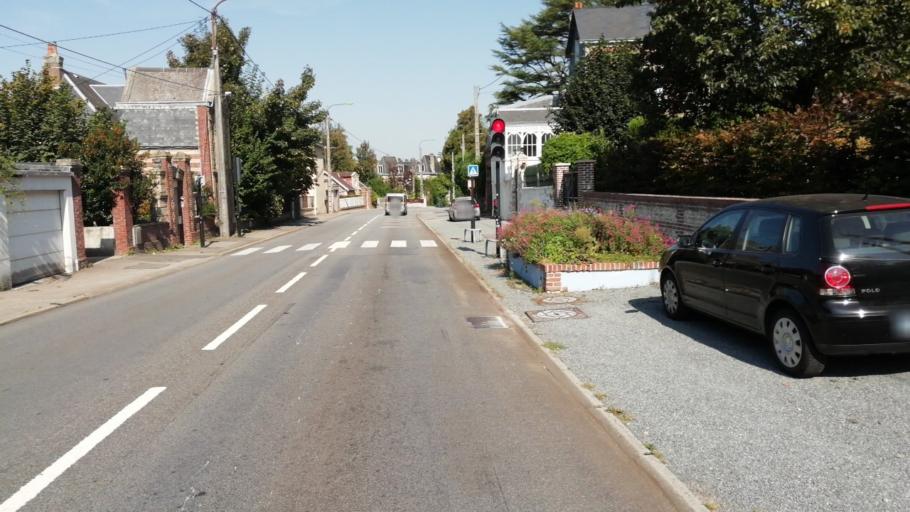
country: FR
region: Haute-Normandie
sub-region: Departement de la Seine-Maritime
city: Montivilliers
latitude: 49.5376
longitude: 0.1869
